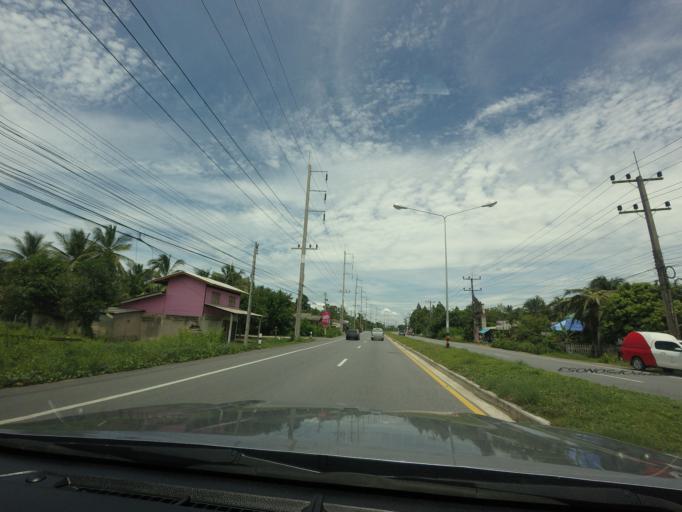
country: TH
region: Songkhla
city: Krasae Sin
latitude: 7.5942
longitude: 100.4038
